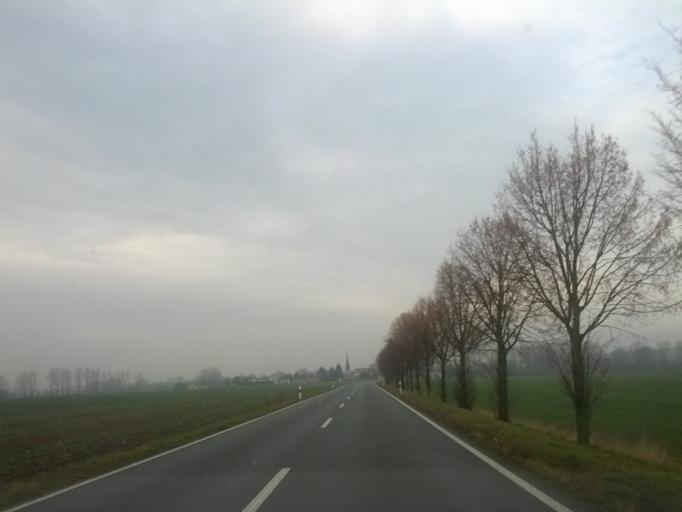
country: DE
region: Thuringia
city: Wangenheim
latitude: 51.0033
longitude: 10.6206
